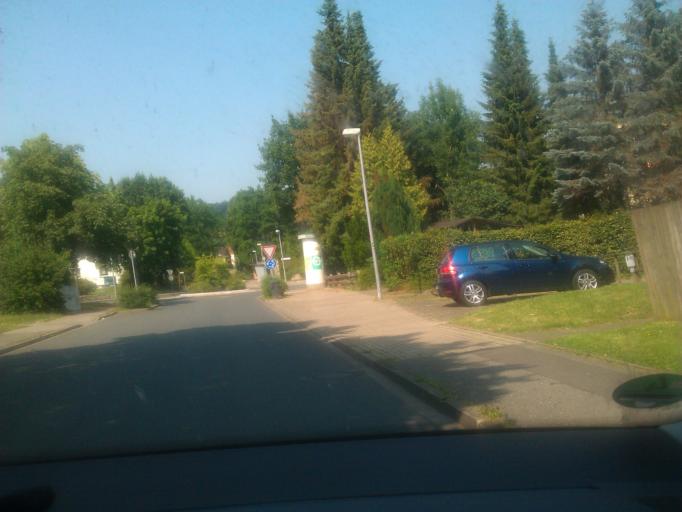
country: DE
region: North Rhine-Westphalia
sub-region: Regierungsbezirk Detmold
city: Lemgo
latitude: 52.0357
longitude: 8.9072
